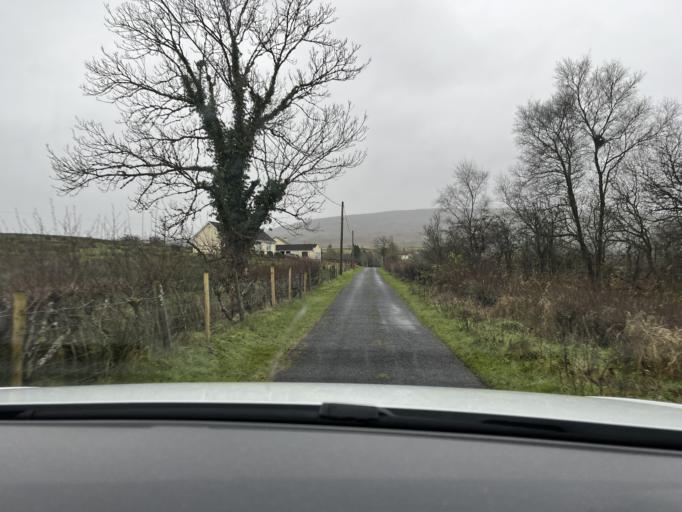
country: IE
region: Connaught
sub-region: County Leitrim
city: Manorhamilton
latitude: 54.2895
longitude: -8.0845
